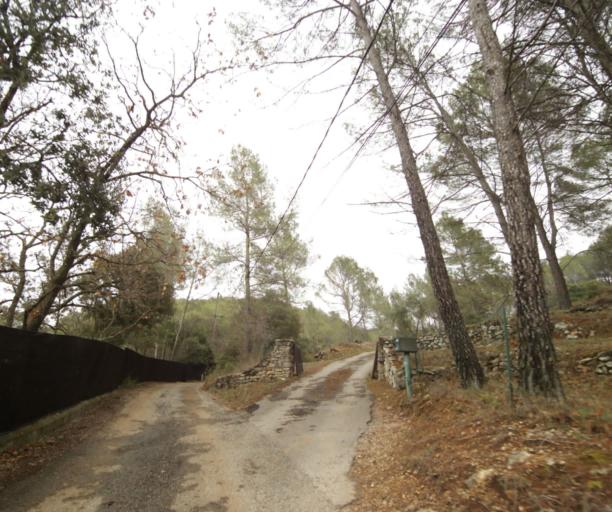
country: FR
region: Provence-Alpes-Cote d'Azur
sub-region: Departement du Var
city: Trans-en-Provence
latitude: 43.5143
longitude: 6.4847
